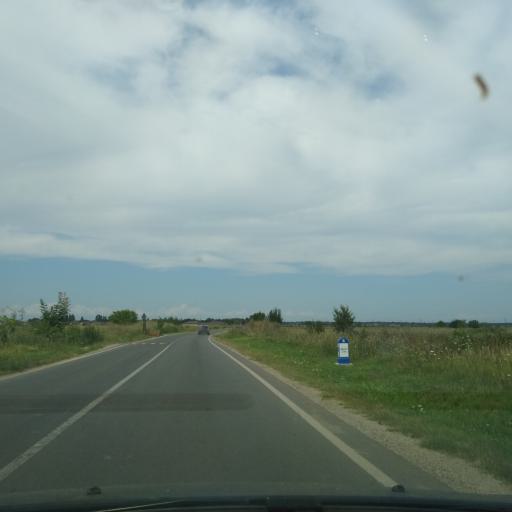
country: RO
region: Ilfov
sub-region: Comuna Balotesti
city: Balotesti
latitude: 44.5996
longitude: 26.1327
